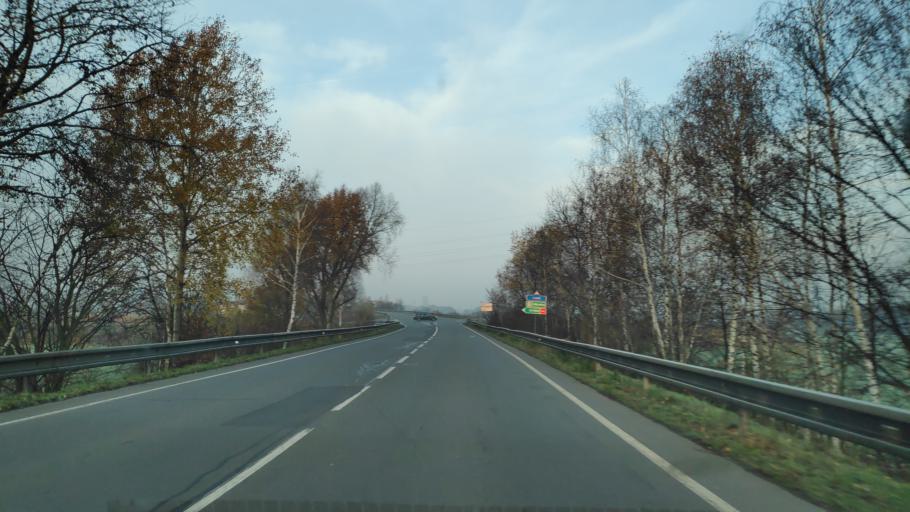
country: CZ
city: Sviadnov
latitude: 49.6919
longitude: 18.3074
